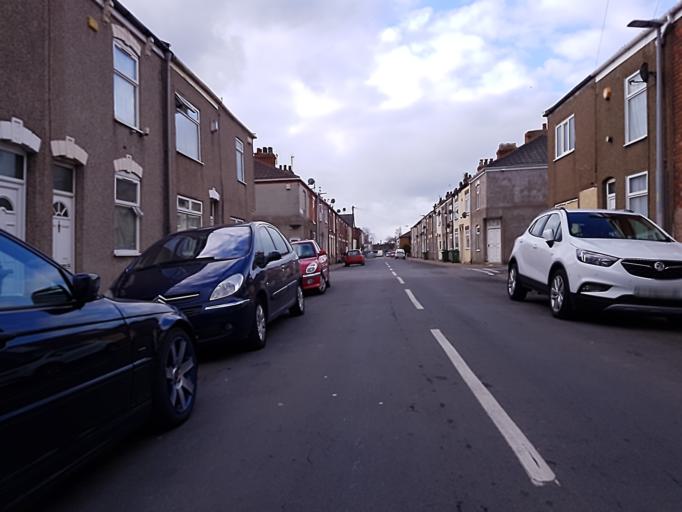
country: GB
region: England
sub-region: North East Lincolnshire
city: Grimsby
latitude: 53.5685
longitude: -0.0617
